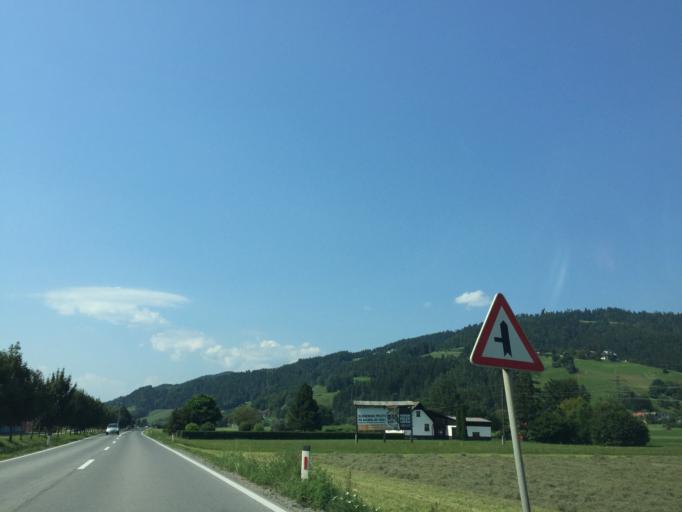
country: SI
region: Slovenj Gradec
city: Pamece
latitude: 46.5336
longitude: 15.0723
